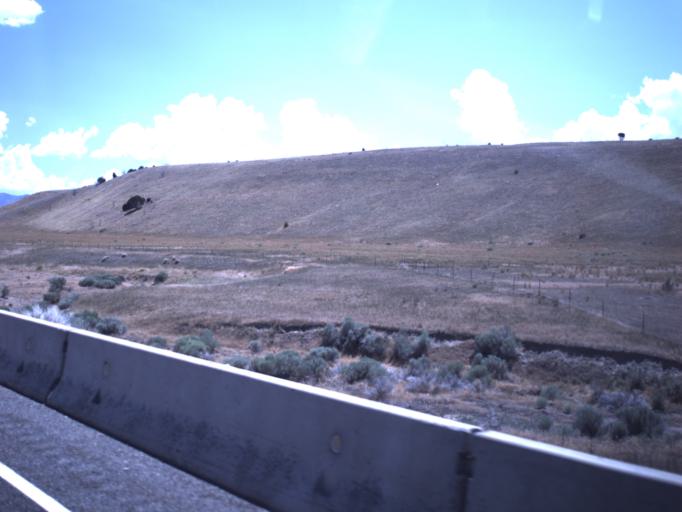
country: US
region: Utah
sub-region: Juab County
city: Nephi
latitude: 39.6359
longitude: -112.1026
